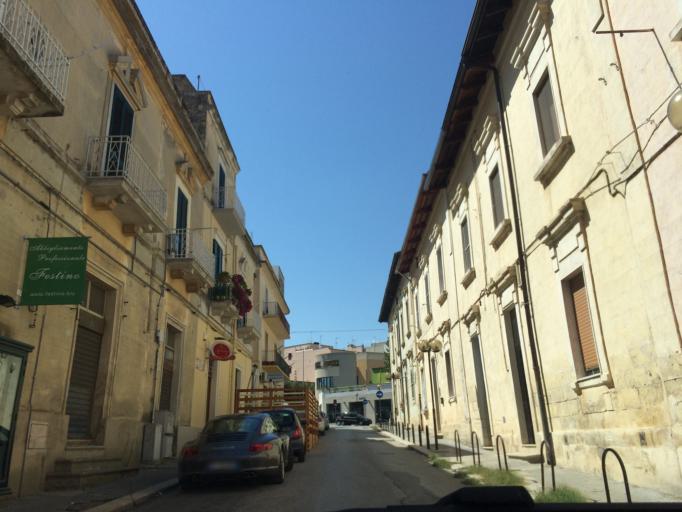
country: IT
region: Basilicate
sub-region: Provincia di Matera
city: Matera
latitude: 40.6705
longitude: 16.6070
